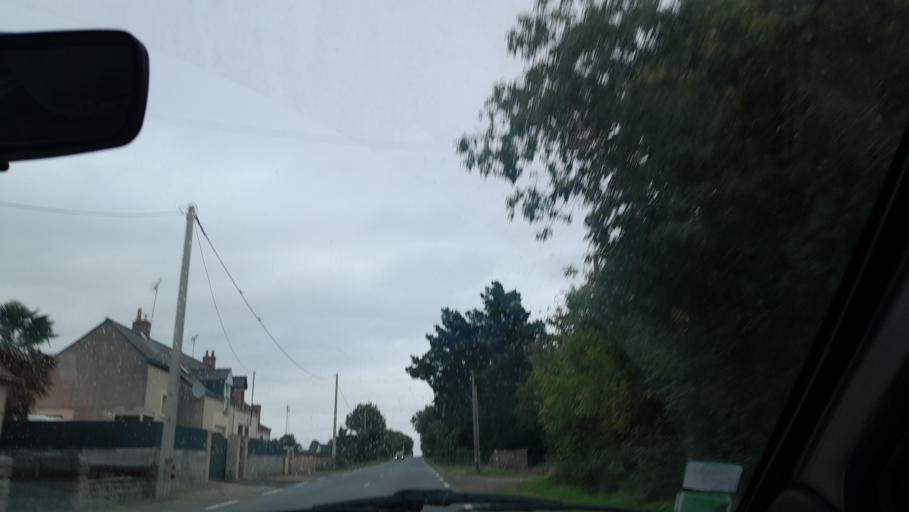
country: FR
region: Pays de la Loire
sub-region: Departement de Maine-et-Loire
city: Pouance
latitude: 47.6664
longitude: -1.1914
